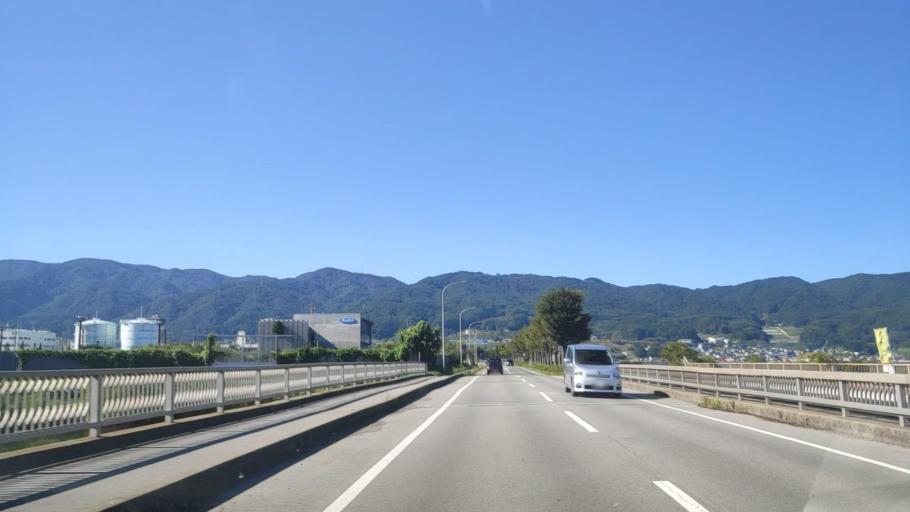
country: JP
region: Nagano
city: Suwa
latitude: 36.0380
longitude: 138.0921
